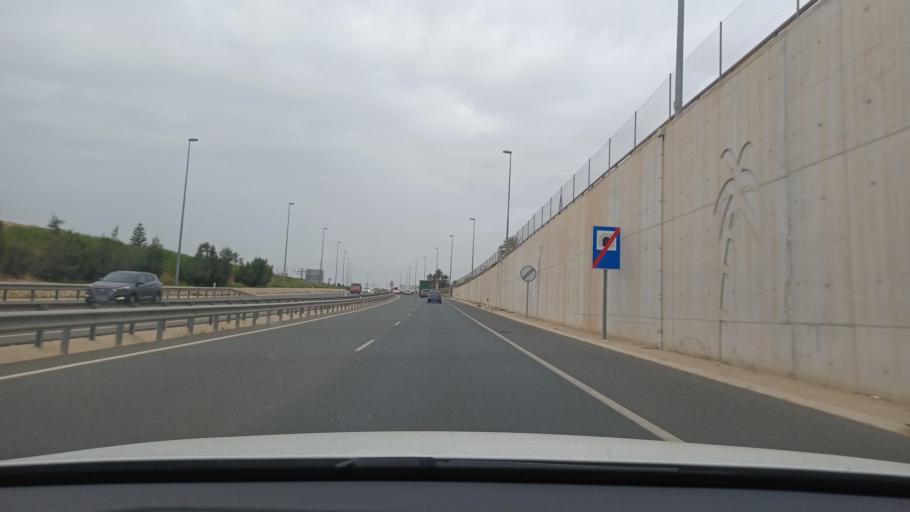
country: ES
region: Valencia
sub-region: Provincia de Alicante
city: Elche
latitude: 38.2574
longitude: -0.6812
